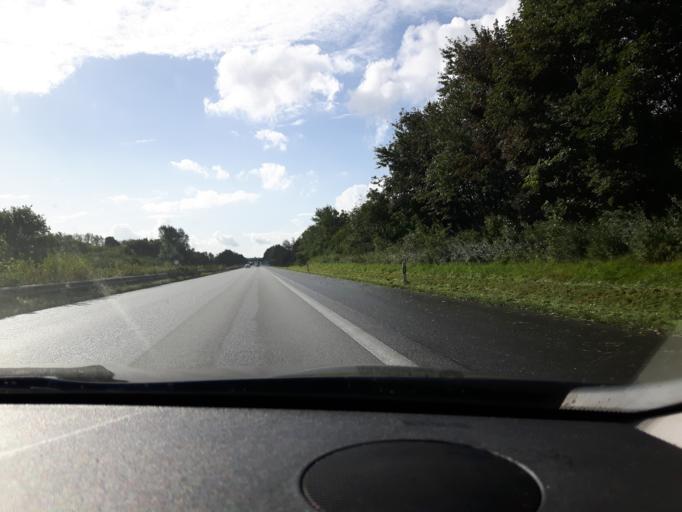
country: DE
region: Schleswig-Holstein
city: Handewitt
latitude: 54.7956
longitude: 9.3333
